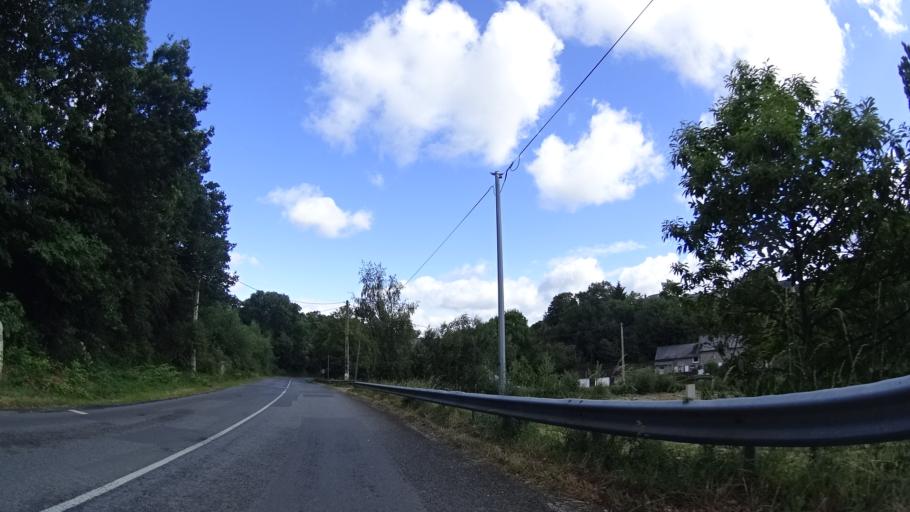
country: FR
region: Brittany
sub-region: Departement d'Ille-et-Vilaine
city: Hede-Bazouges
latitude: 48.2909
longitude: -1.8012
